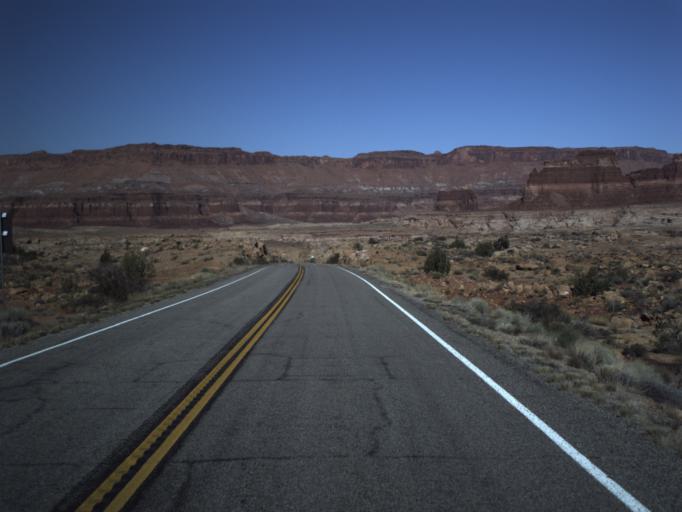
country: US
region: Utah
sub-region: San Juan County
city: Blanding
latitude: 37.8804
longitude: -110.3550
